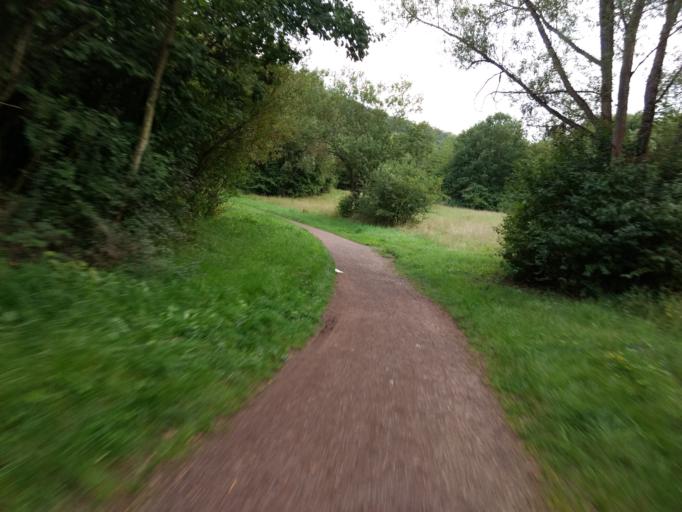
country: DE
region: Saarland
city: Wallerfangen
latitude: 49.3483
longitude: 6.7040
